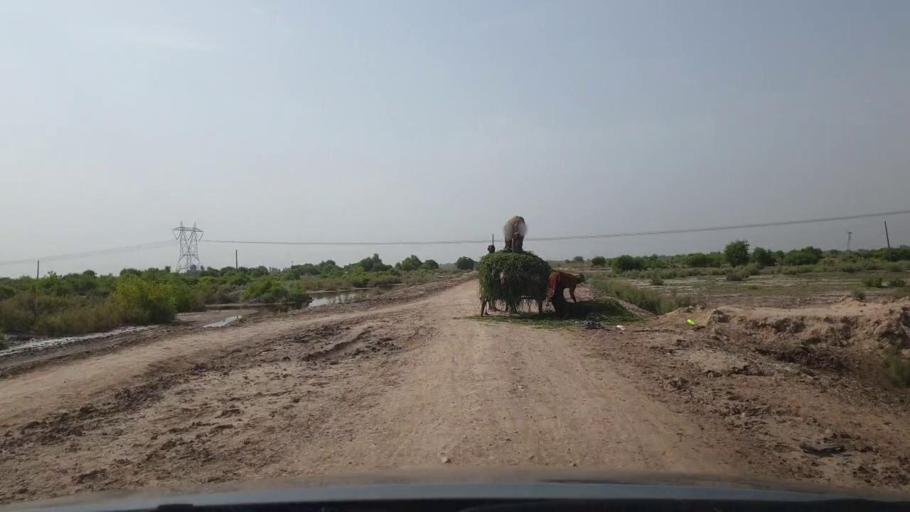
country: PK
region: Sindh
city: Rohri
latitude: 27.6769
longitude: 69.0119
